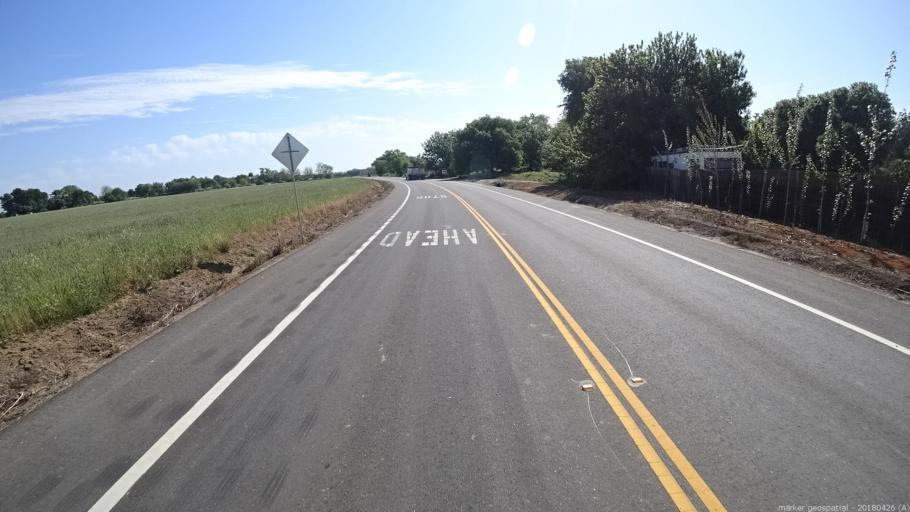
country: US
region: California
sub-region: Yolo County
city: West Sacramento
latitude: 38.5200
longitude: -121.5552
